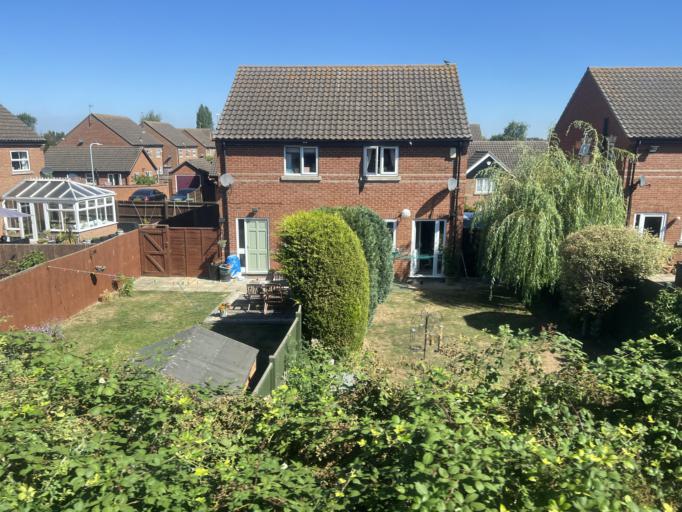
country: GB
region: England
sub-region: Lincolnshire
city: Boston
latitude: 52.9703
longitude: -0.0461
